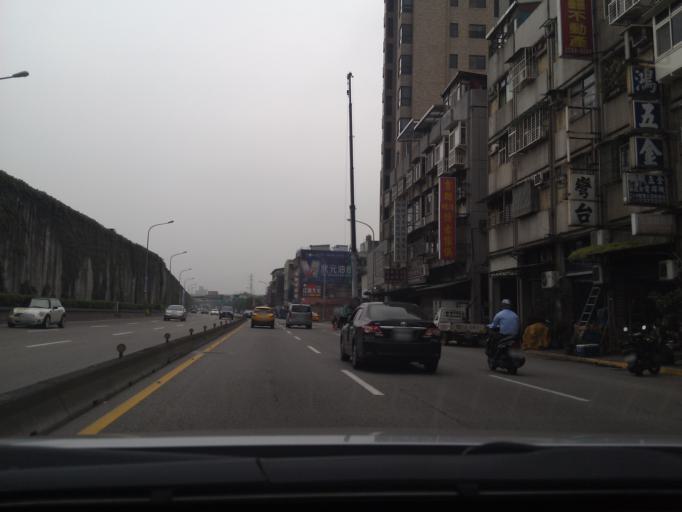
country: TW
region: Taipei
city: Taipei
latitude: 25.0701
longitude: 121.5093
